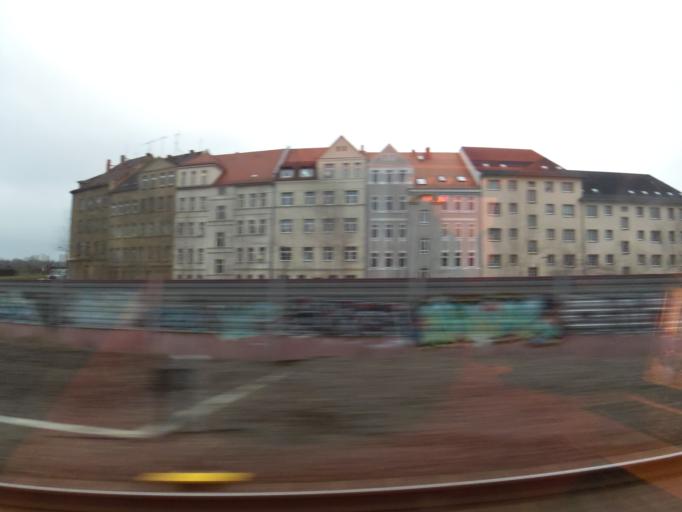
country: DE
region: Saxony
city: Leipzig
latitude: 51.3450
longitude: 12.4258
